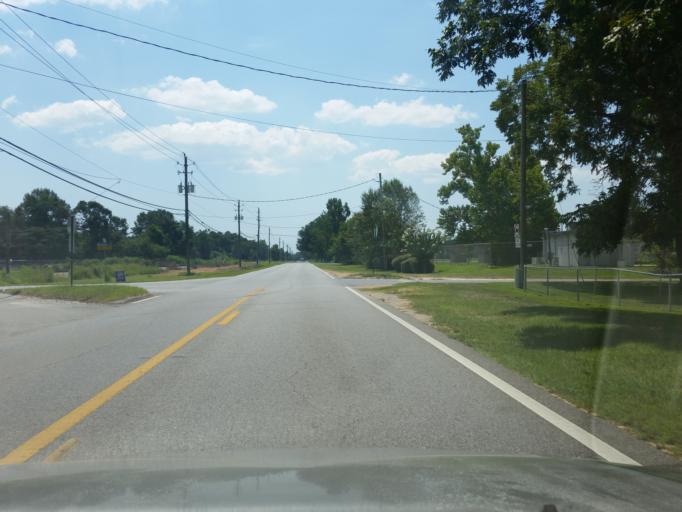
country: US
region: Florida
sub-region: Escambia County
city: Cantonment
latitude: 30.6018
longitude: -87.3137
